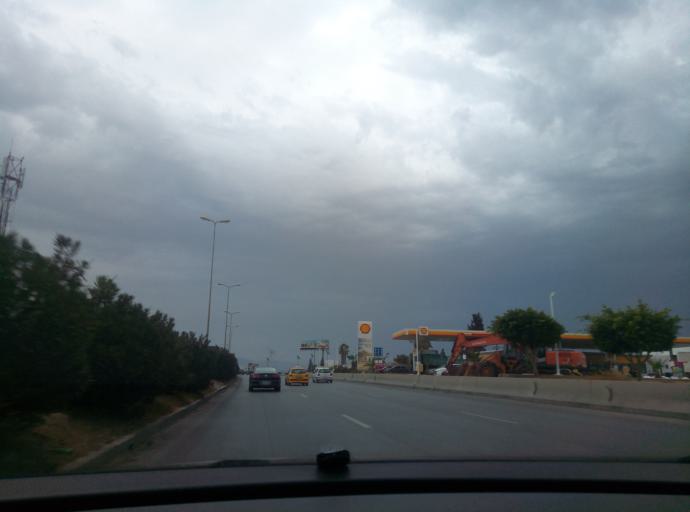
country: TN
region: Bin 'Arus
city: Ben Arous
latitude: 36.7342
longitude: 10.2240
